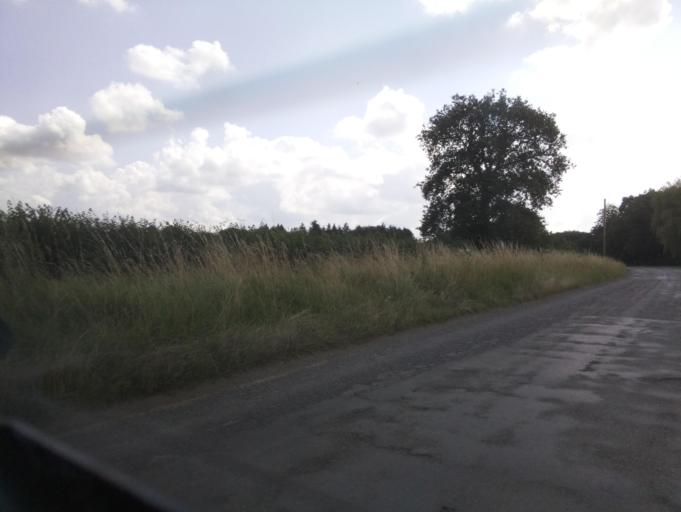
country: GB
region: England
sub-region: Wiltshire
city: Hankerton
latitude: 51.5851
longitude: -2.0151
